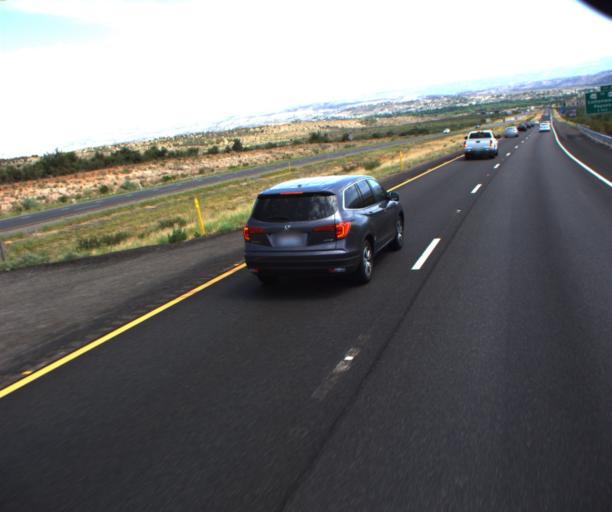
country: US
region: Arizona
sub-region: Yavapai County
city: Camp Verde
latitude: 34.5652
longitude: -111.8993
